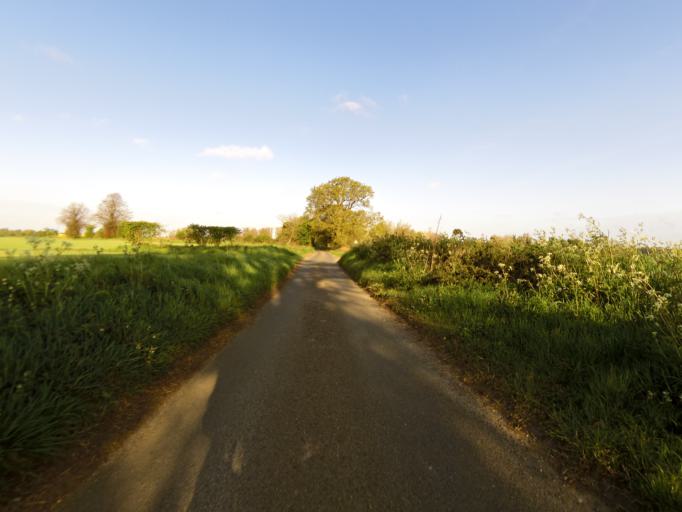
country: GB
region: England
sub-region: Suffolk
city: Bramford
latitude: 52.0453
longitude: 1.0686
